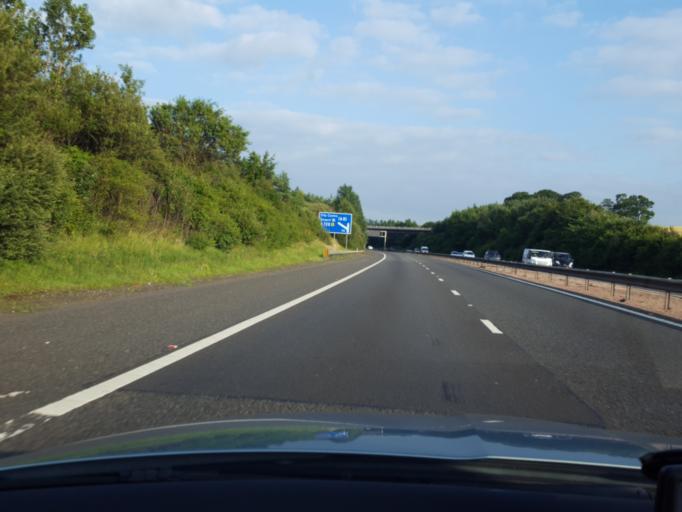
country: GB
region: Scotland
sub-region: Edinburgh
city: Ratho
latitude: 55.9241
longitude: -3.3458
